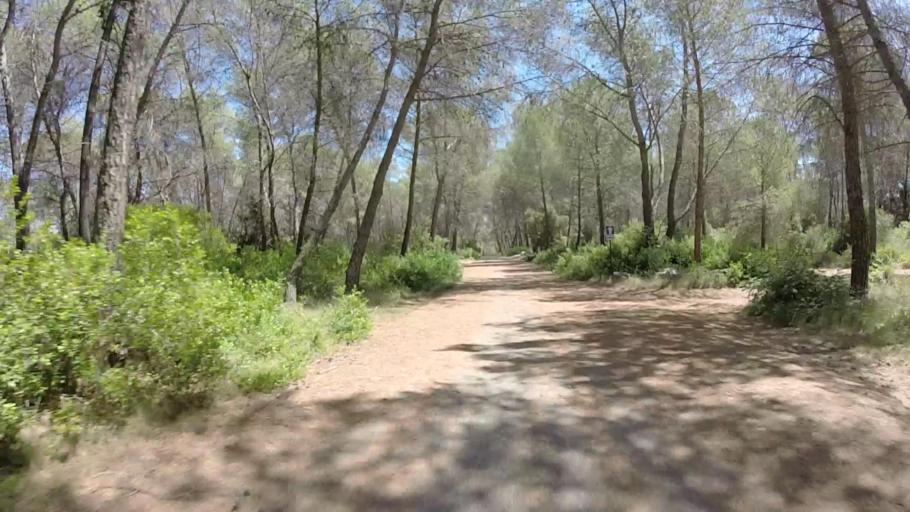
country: FR
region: Provence-Alpes-Cote d'Azur
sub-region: Departement des Alpes-Maritimes
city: Vallauris
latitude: 43.6085
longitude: 7.0486
